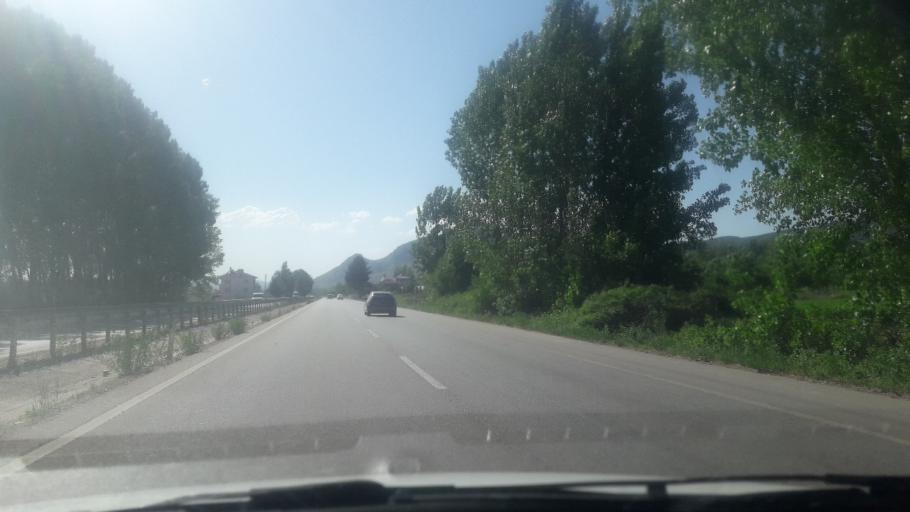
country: TR
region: Tokat
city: Dokmetepe
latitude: 40.3176
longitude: 36.2437
